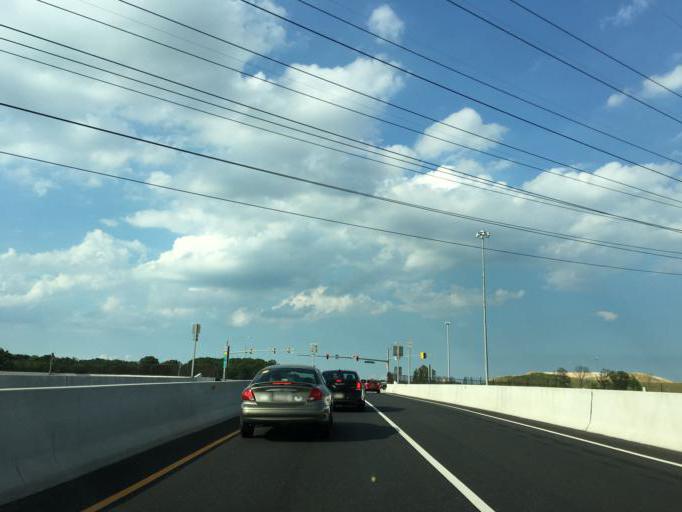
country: US
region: Maryland
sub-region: Baltimore County
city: White Marsh
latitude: 39.3784
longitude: -76.4498
